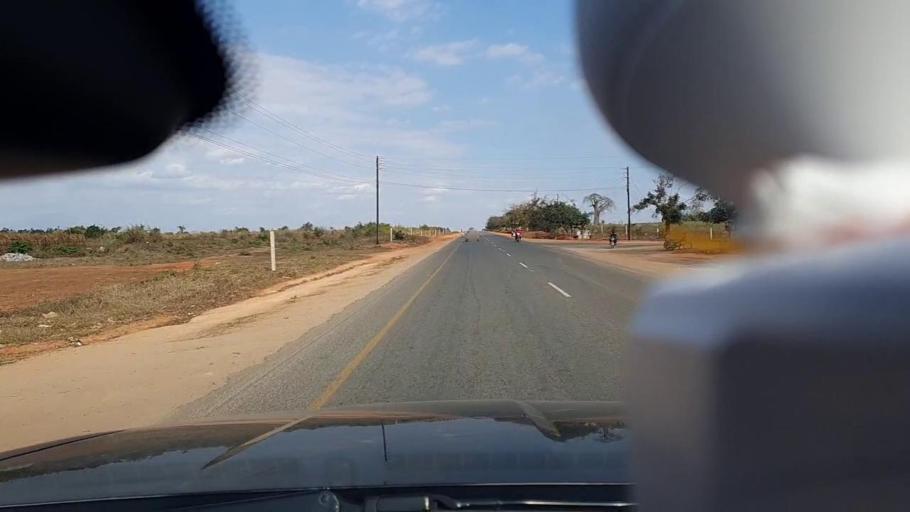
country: MZ
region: Nampula
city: Nampula
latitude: -15.1503
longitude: 39.3008
